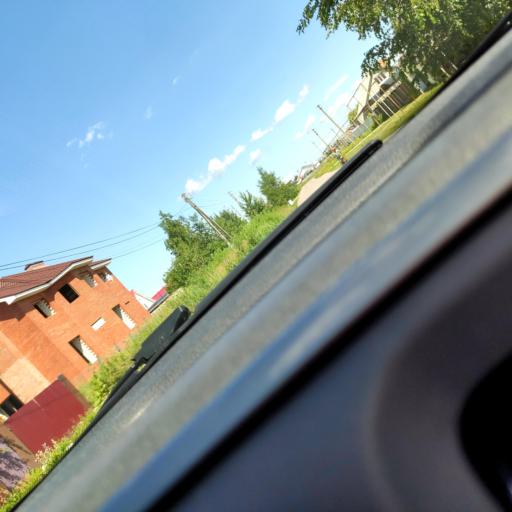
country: RU
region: Samara
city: Podstepki
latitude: 53.5216
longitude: 49.1508
